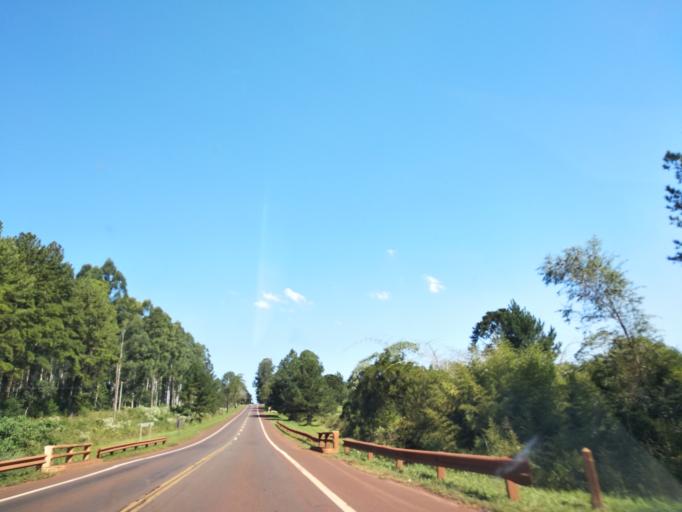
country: AR
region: Misiones
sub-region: Departamento de Montecarlo
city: Montecarlo
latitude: -26.5565
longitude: -54.7248
